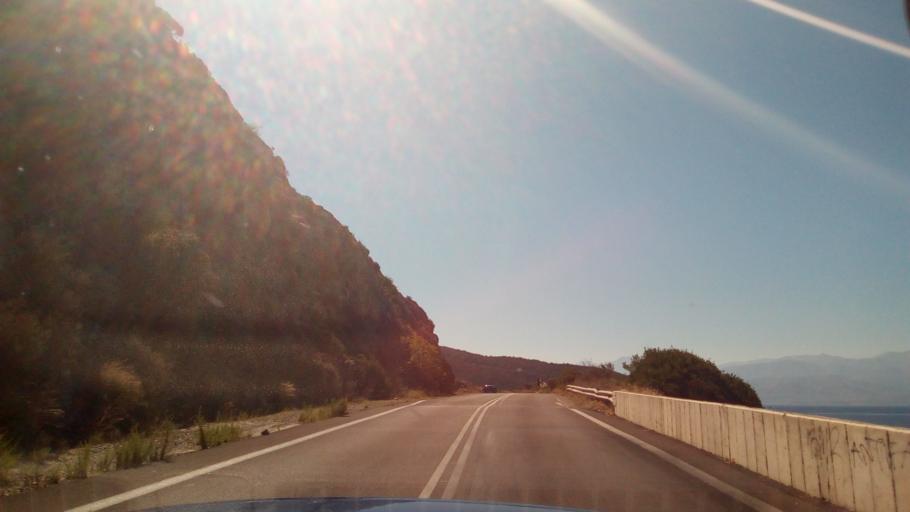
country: GR
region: West Greece
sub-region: Nomos Achaias
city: Kamarai
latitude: 38.3835
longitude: 22.0652
